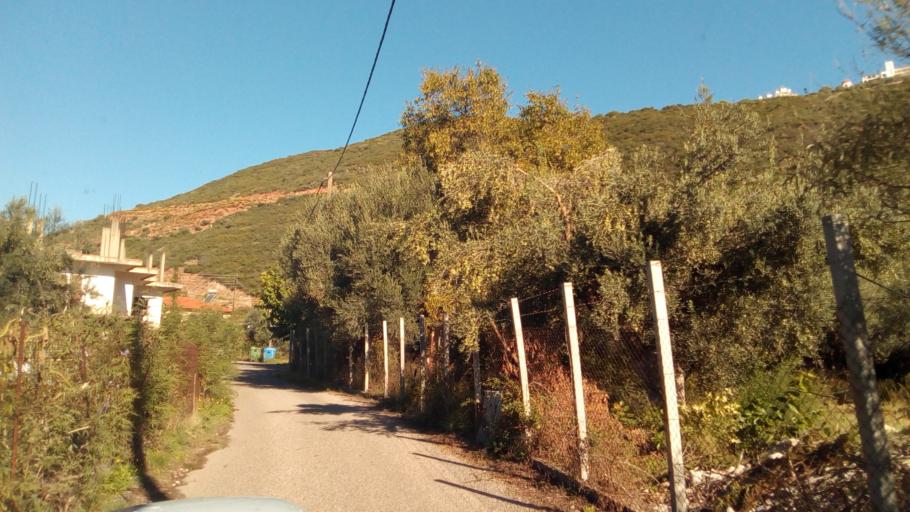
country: GR
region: West Greece
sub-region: Nomos Aitolias kai Akarnanias
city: Nafpaktos
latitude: 38.4103
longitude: 21.8514
